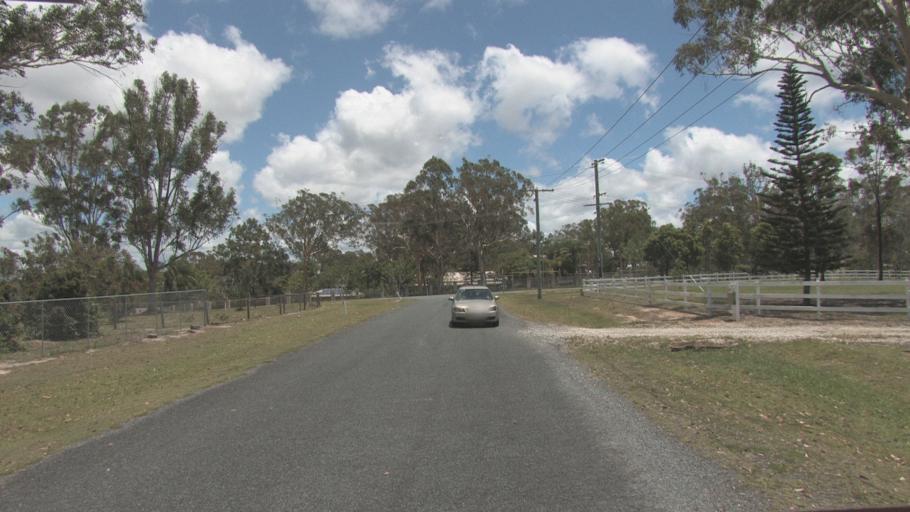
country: AU
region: Queensland
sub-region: Redland
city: Redland Bay
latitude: -27.6608
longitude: 153.2779
